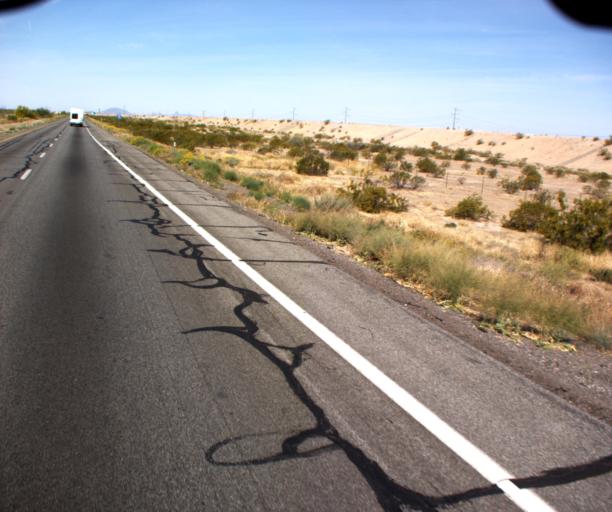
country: US
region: Arizona
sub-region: Maricopa County
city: Buckeye
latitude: 33.4414
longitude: -112.6861
